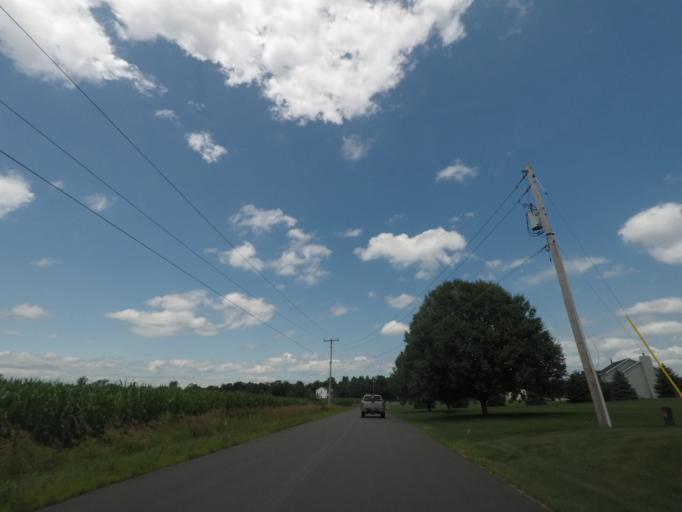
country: US
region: New York
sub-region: Rensselaer County
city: East Greenbush
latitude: 42.5387
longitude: -73.6919
